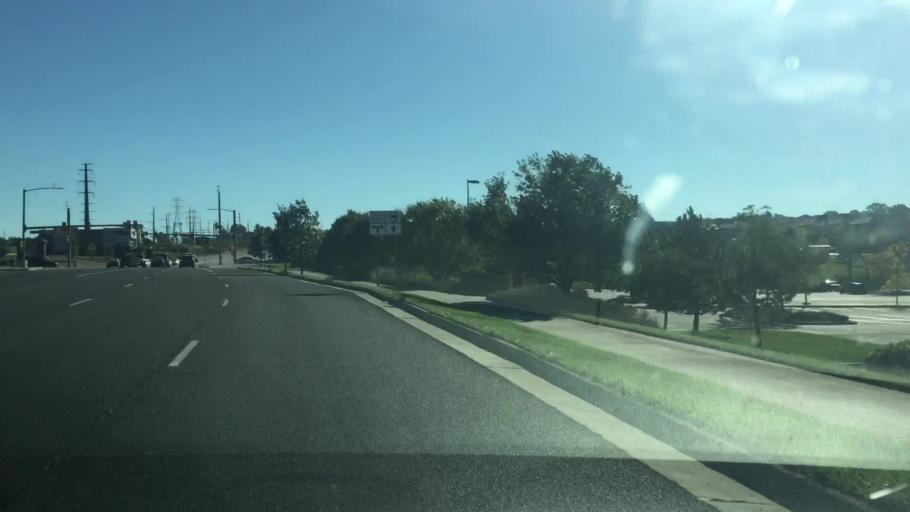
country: US
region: Colorado
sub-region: Douglas County
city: Parker
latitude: 39.5100
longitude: -104.7657
